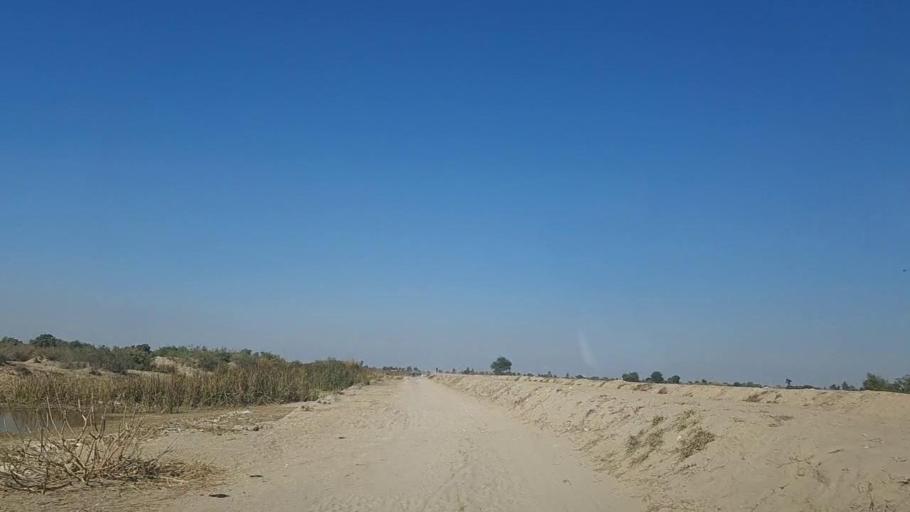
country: PK
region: Sindh
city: Sanghar
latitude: 26.2101
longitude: 68.9294
